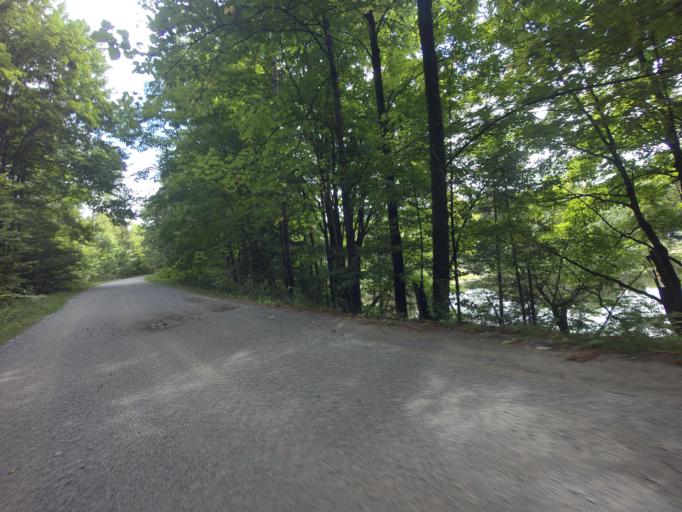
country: CA
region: Ontario
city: Omemee
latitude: 44.7616
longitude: -78.6663
